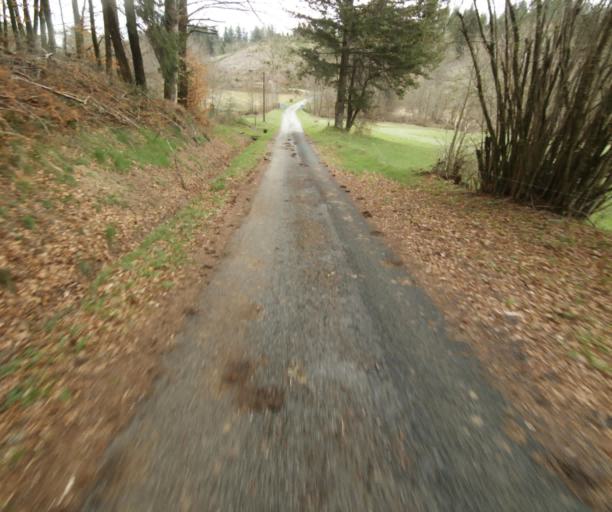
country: FR
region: Limousin
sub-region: Departement de la Correze
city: Correze
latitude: 45.2656
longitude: 1.9574
